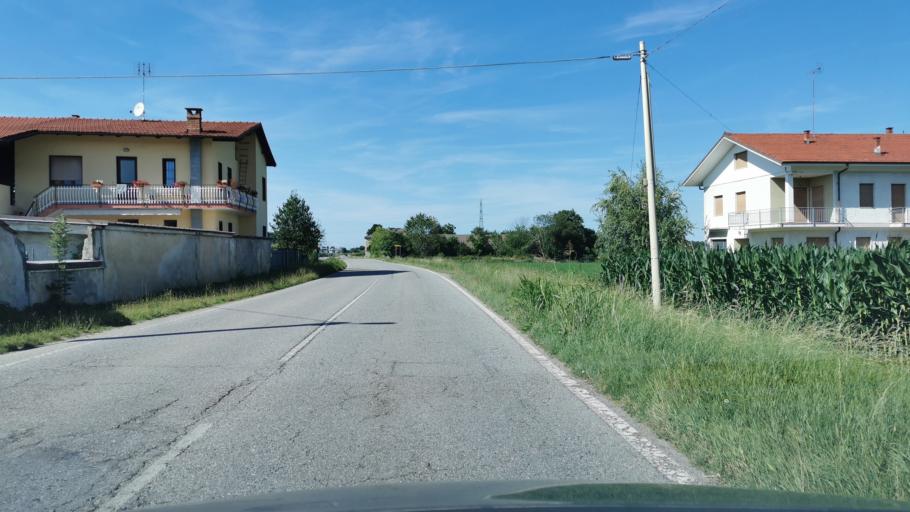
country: IT
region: Piedmont
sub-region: Provincia di Cuneo
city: Boves
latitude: 44.3477
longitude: 7.5583
